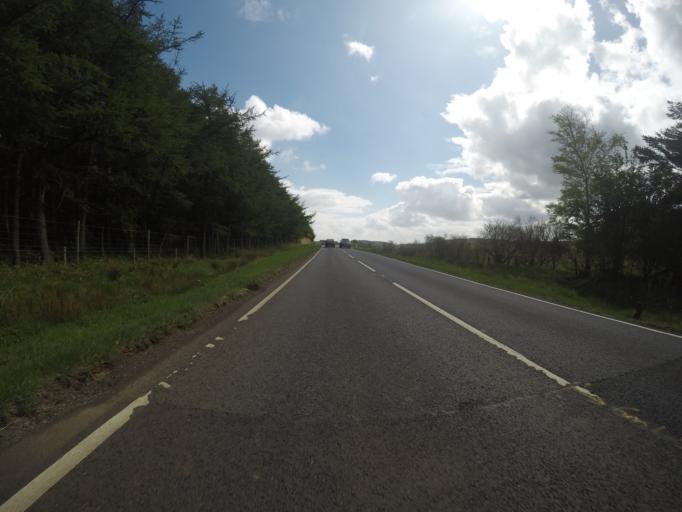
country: GB
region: Scotland
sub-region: Highland
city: Portree
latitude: 57.5289
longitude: -6.3485
